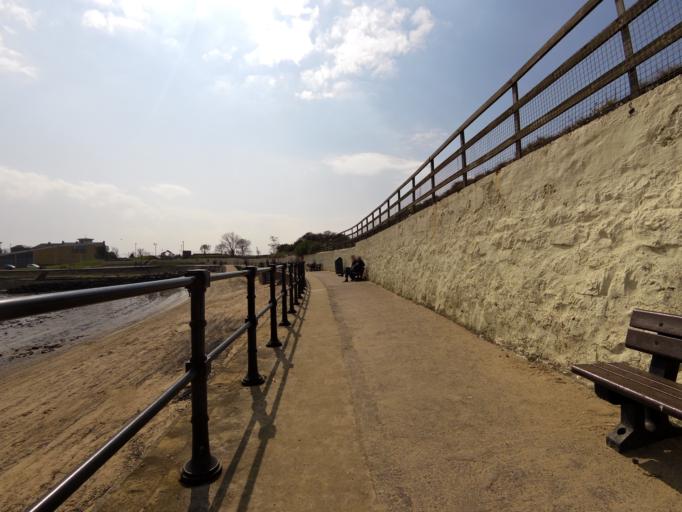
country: GB
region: Scotland
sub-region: Fife
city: Burntisland
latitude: 56.0612
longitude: -3.2252
